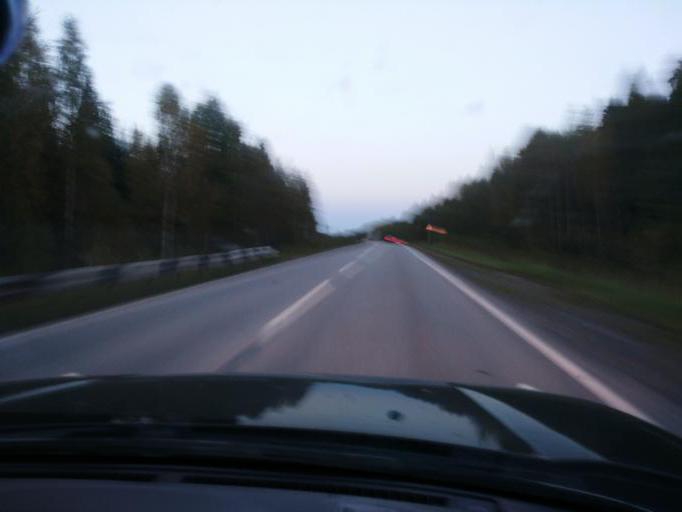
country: RU
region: Perm
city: Verkhnechusovskiye Gorodki
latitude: 58.2488
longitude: 57.0173
